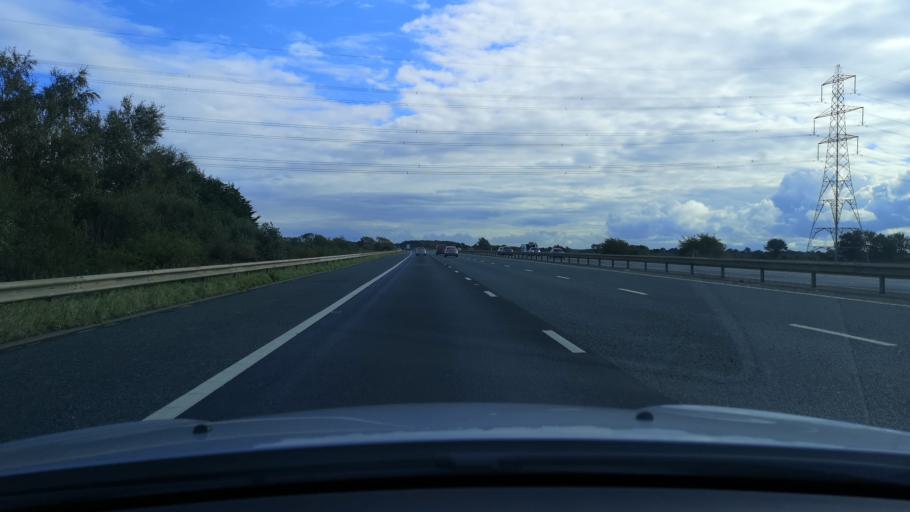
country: GB
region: England
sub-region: East Riding of Yorkshire
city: Pollington
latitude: 53.6810
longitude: -1.0533
